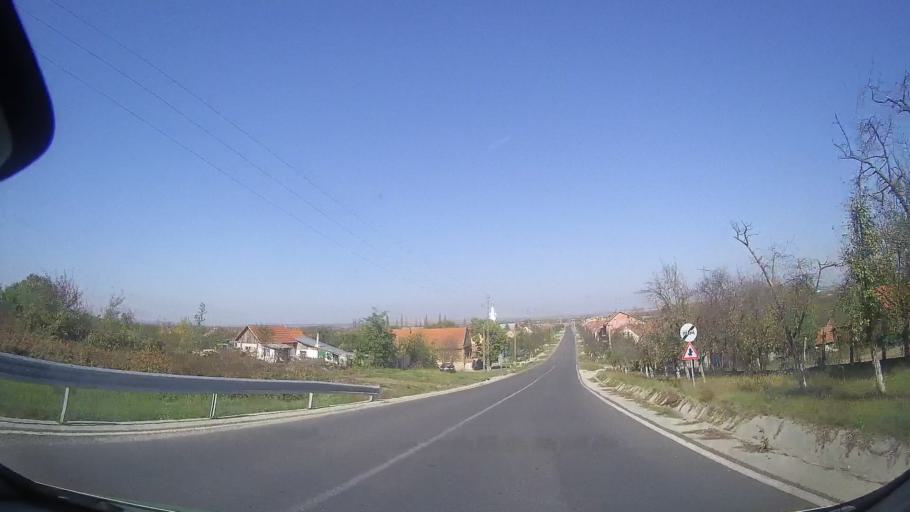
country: RO
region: Timis
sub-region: Comuna Costeiu
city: Costeiu
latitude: 45.7743
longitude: 21.8499
